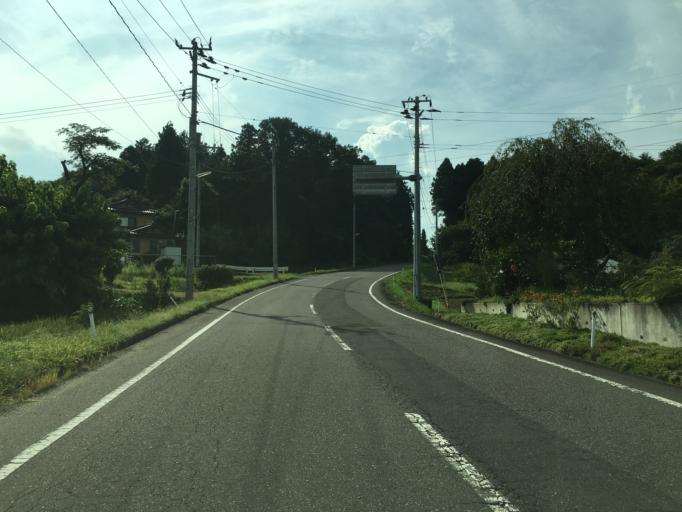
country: JP
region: Fukushima
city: Sukagawa
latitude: 37.3281
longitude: 140.4339
